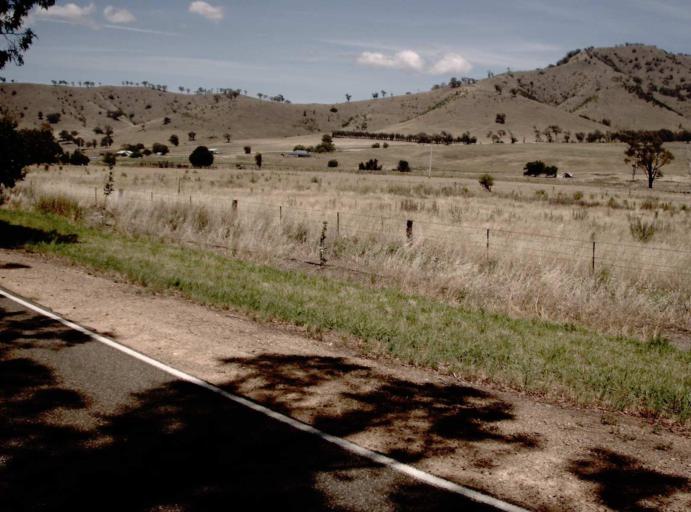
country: AU
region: Victoria
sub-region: East Gippsland
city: Bairnsdale
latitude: -37.2388
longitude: 147.7138
